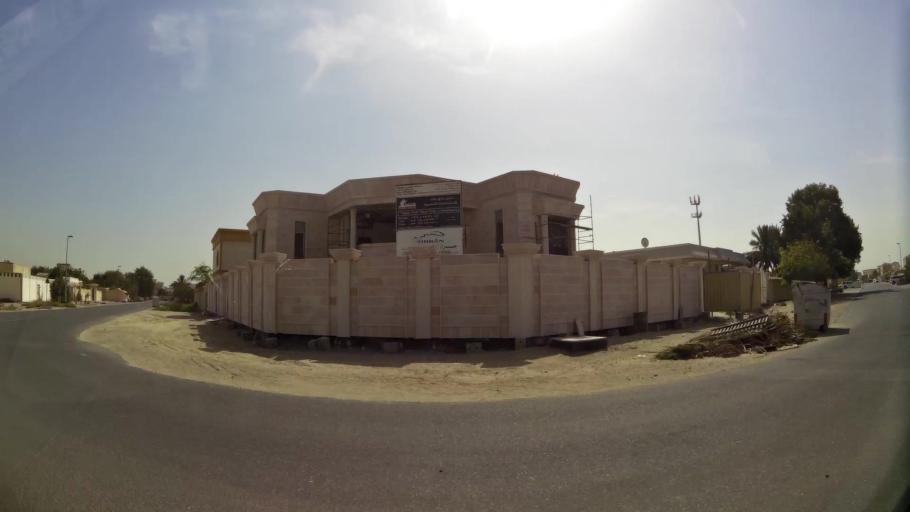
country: AE
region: Ash Shariqah
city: Sharjah
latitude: 25.2692
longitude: 55.4009
